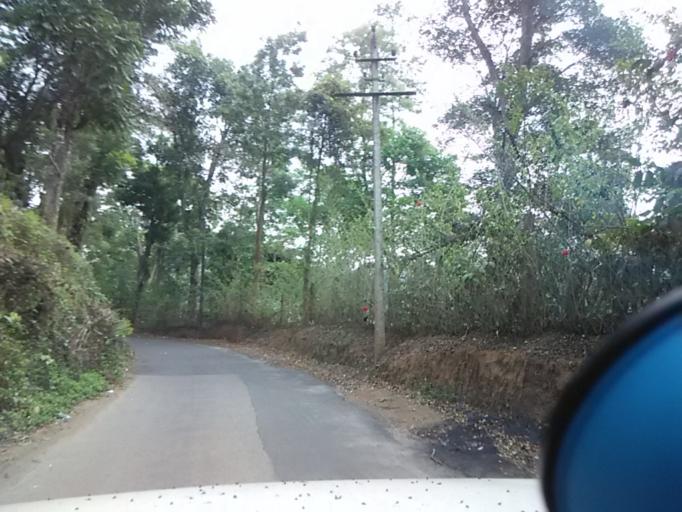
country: IN
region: Karnataka
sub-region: Kodagu
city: Virarajendrapet
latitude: 12.2091
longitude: 75.7344
